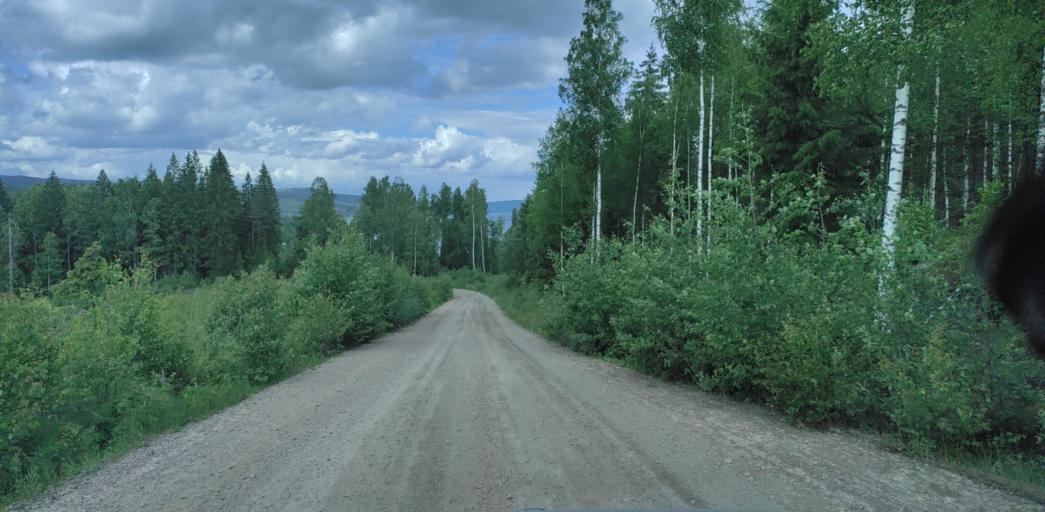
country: SE
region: Vaermland
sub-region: Munkfors Kommun
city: Munkfors
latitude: 59.9666
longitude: 13.4239
